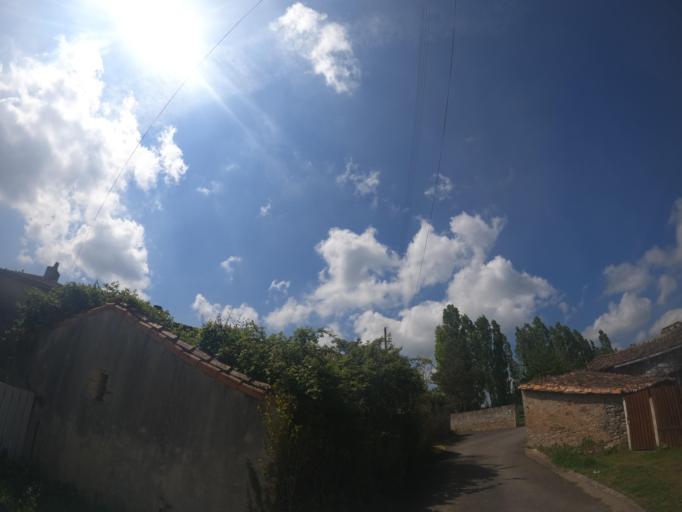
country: FR
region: Poitou-Charentes
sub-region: Departement des Deux-Sevres
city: Saint-Varent
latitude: 46.8564
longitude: -0.2011
